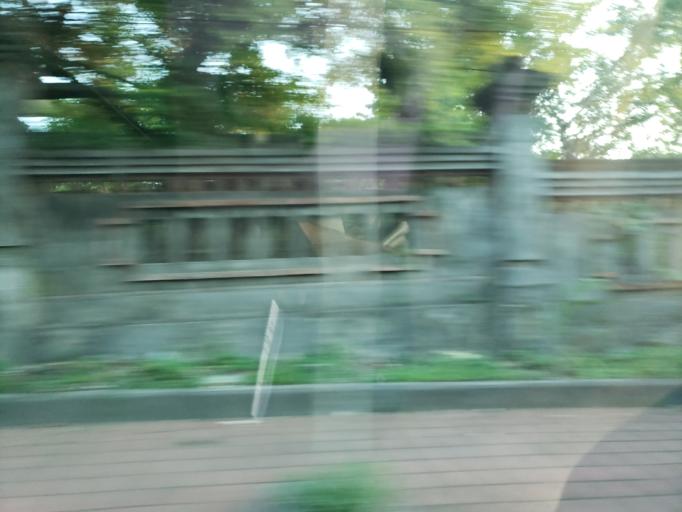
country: ID
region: Bali
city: Jimbaran
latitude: -8.7999
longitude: 115.1686
